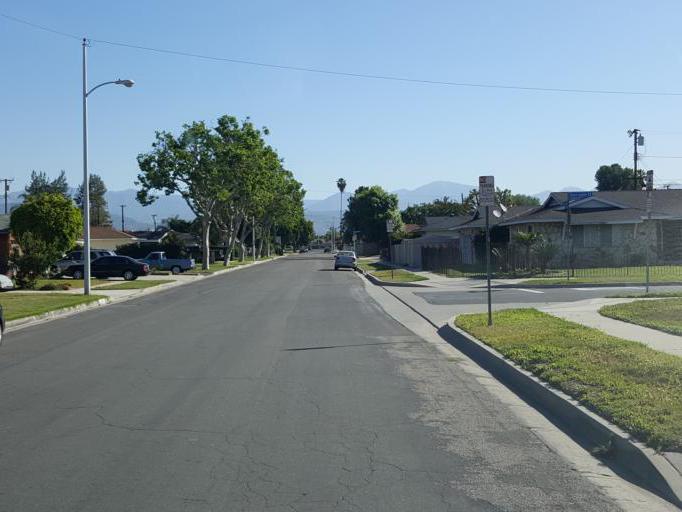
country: US
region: California
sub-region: Los Angeles County
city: West Puente Valley
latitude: 34.0595
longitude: -117.9685
